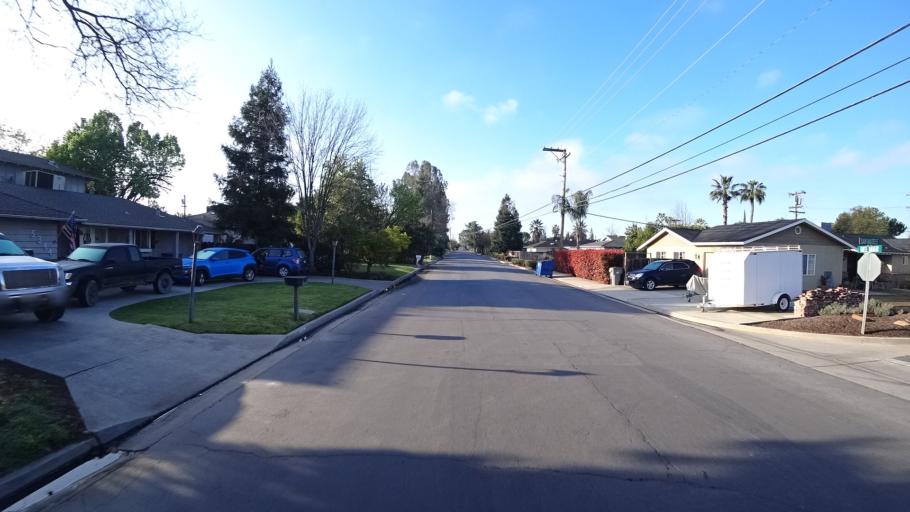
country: US
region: California
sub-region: Fresno County
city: Fresno
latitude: 36.8147
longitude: -119.7949
